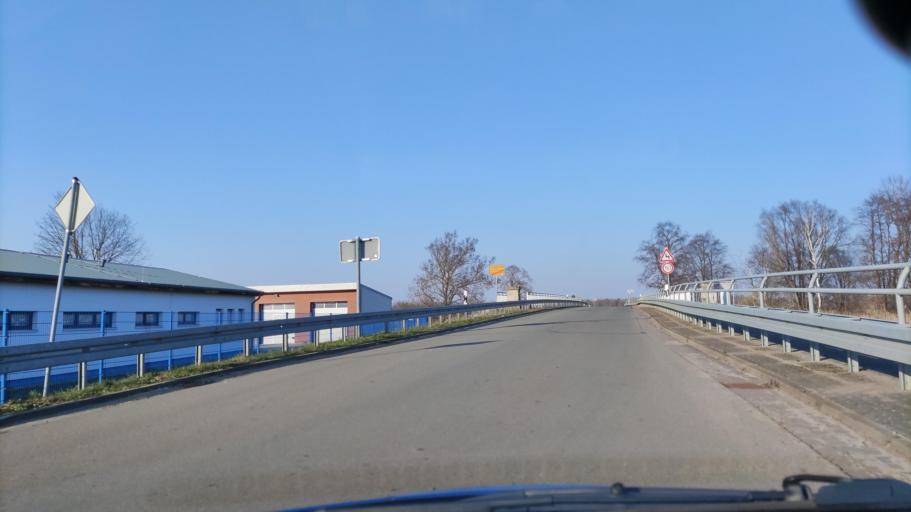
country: DE
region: Saxony-Anhalt
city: Seehausen
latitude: 52.9000
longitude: 11.7543
